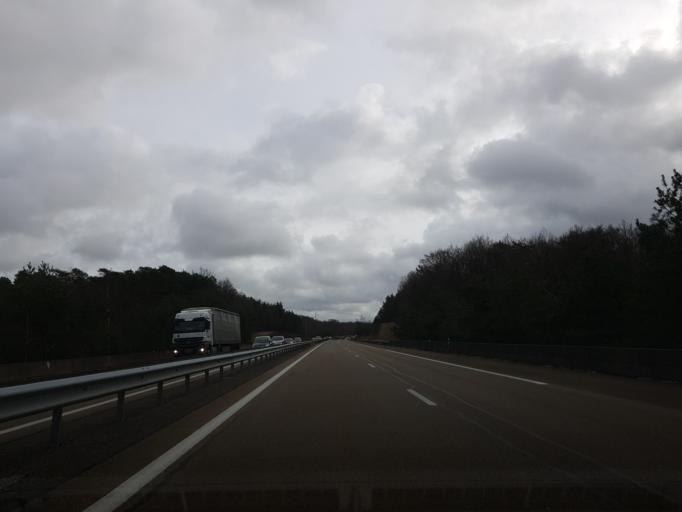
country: FR
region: Champagne-Ardenne
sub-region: Departement de la Haute-Marne
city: Chamarandes-Choignes
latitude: 48.0028
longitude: 5.1137
